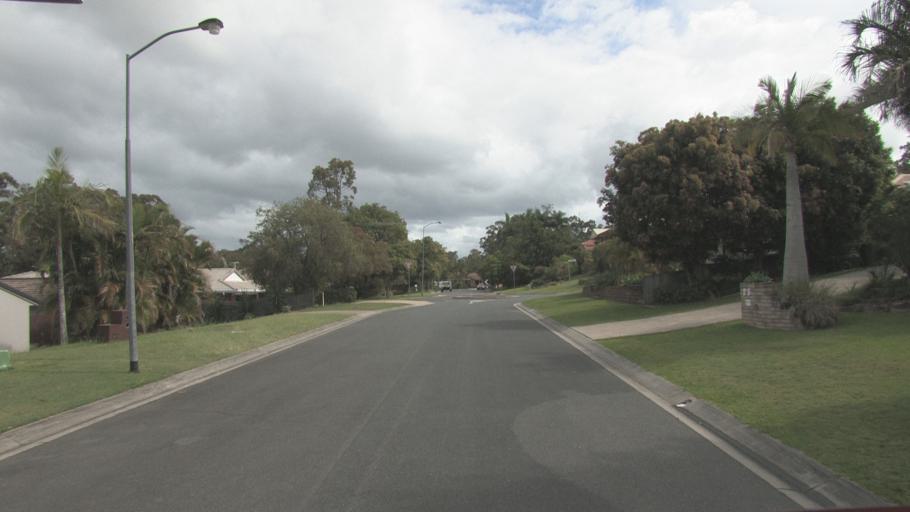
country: AU
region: Queensland
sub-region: Logan
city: Beenleigh
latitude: -27.6634
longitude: 153.2013
